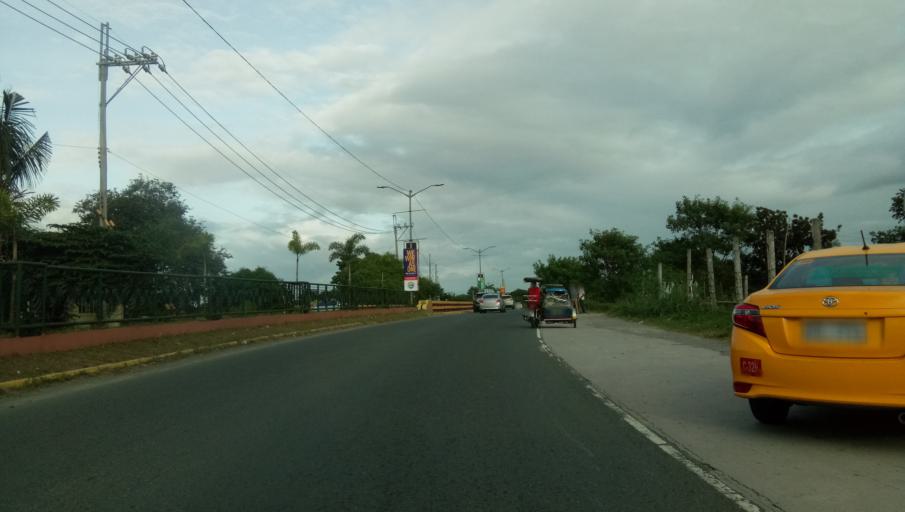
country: PH
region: Calabarzon
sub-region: Province of Cavite
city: Dasmarinas
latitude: 14.3731
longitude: 120.9414
